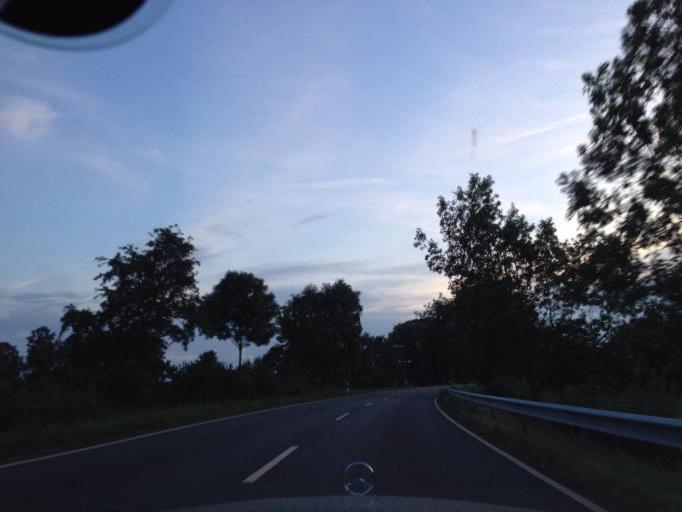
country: DE
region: Schleswig-Holstein
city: Grosshansdorf
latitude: 53.6838
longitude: 10.2720
